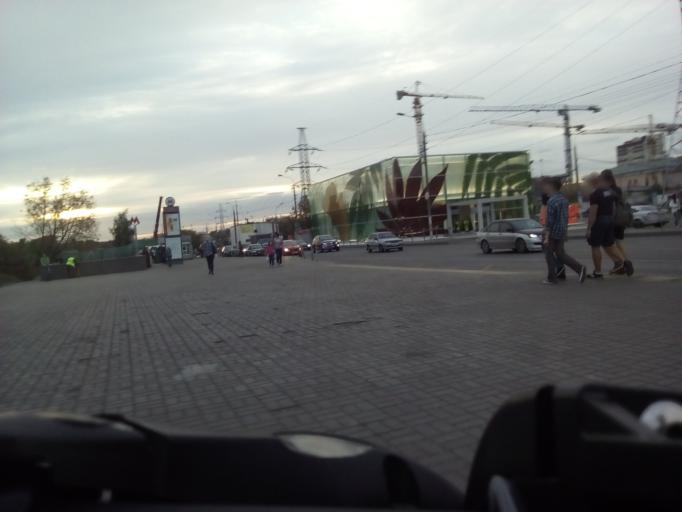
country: RU
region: Moscow
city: Sviblovo
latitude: 55.8460
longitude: 37.6394
